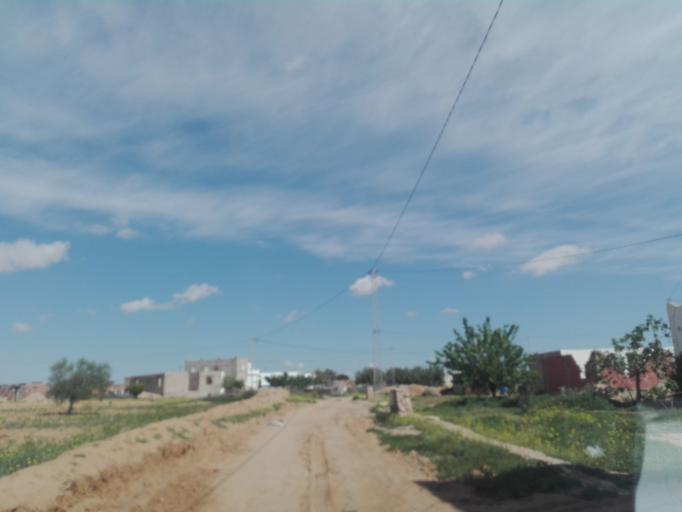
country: TN
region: Safaqis
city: Sfax
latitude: 34.7317
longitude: 10.5057
